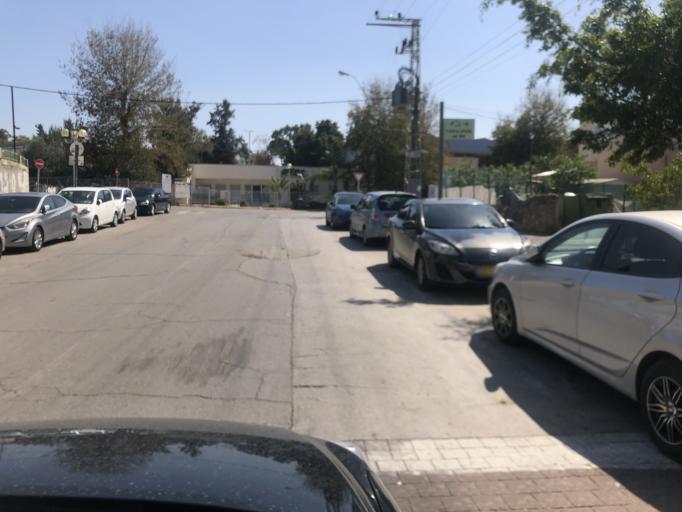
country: IL
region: Tel Aviv
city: Holon
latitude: 32.0047
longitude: 34.7633
